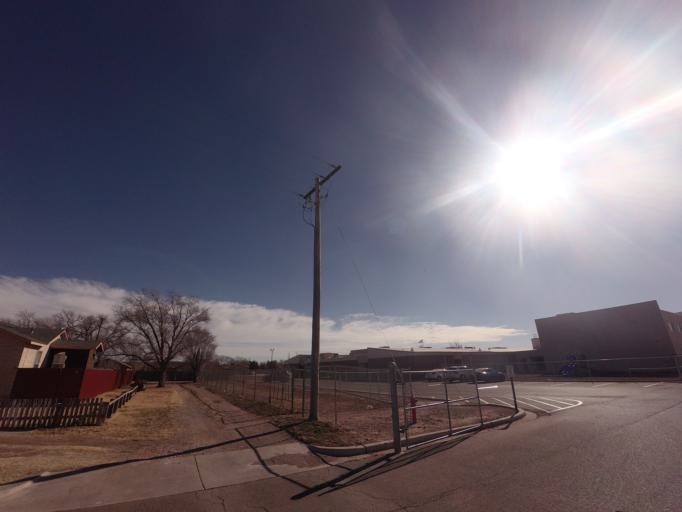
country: US
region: New Mexico
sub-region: Curry County
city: Clovis
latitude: 34.4033
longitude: -103.2180
